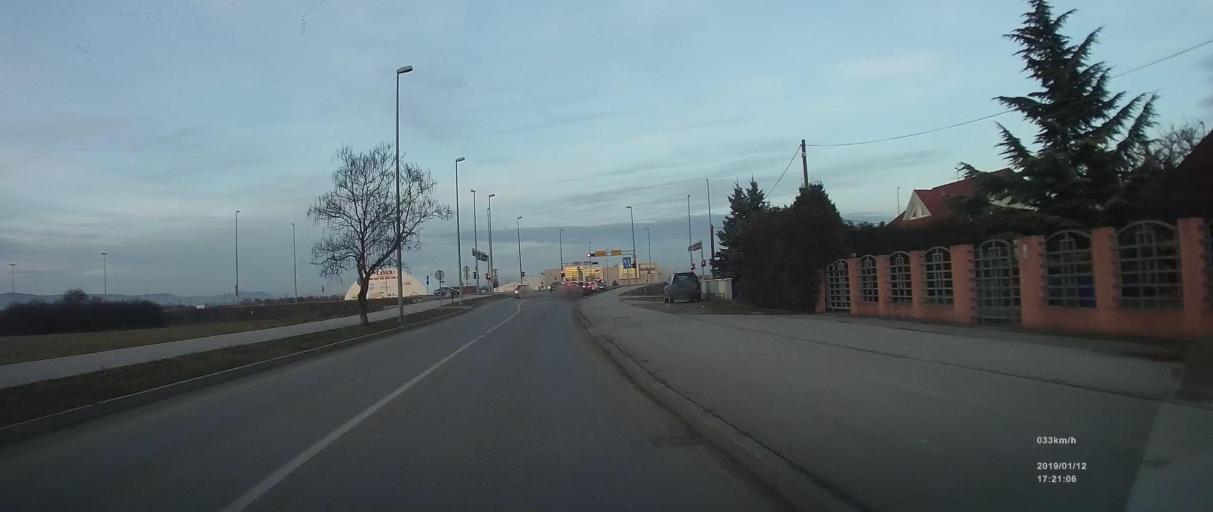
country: HR
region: Zagrebacka
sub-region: Grad Velika Gorica
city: Velika Gorica
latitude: 45.7194
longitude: 16.0782
